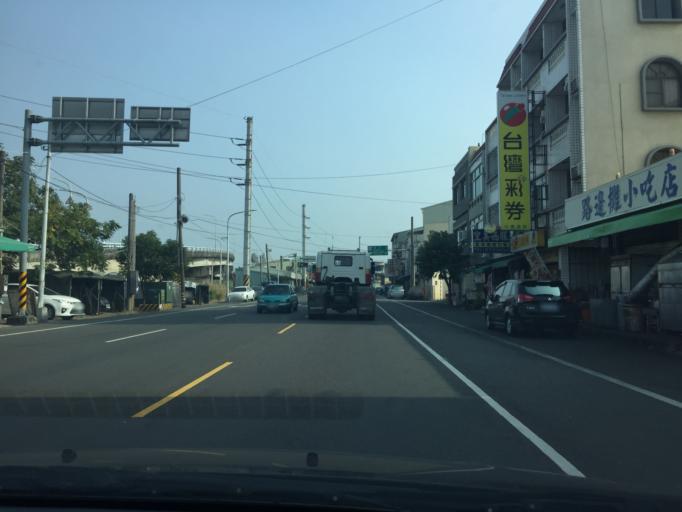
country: TW
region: Taiwan
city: Xinying
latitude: 23.1980
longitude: 120.3172
